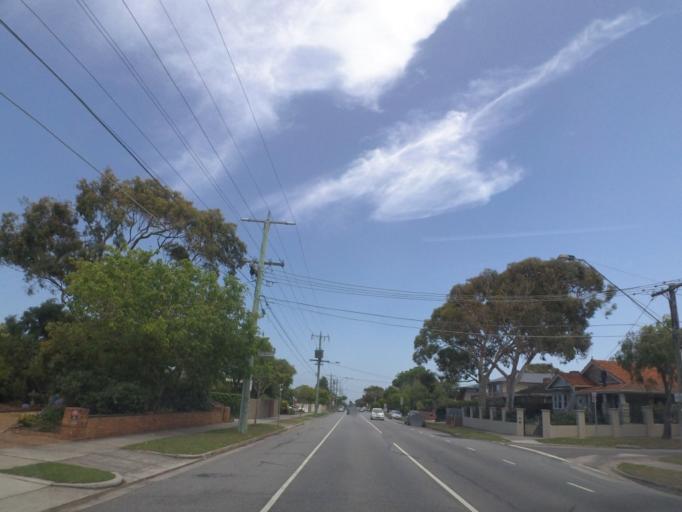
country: AU
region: Victoria
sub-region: Bayside
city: Black Rock
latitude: -37.9764
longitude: 145.0228
